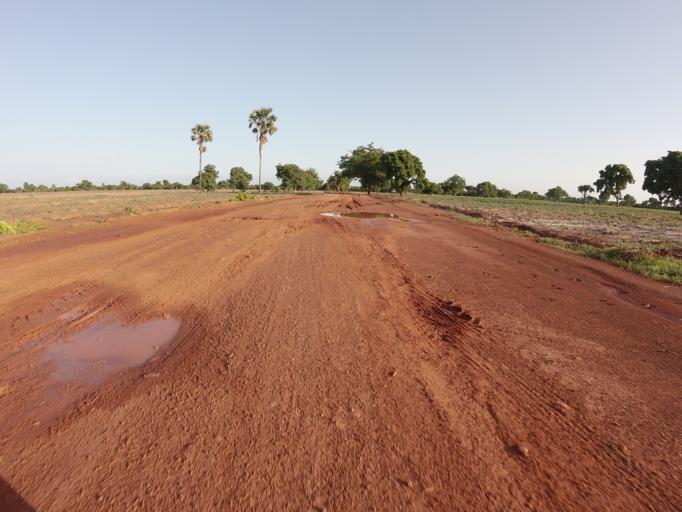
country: TG
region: Savanes
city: Sansanne-Mango
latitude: 10.3450
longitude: -0.0926
